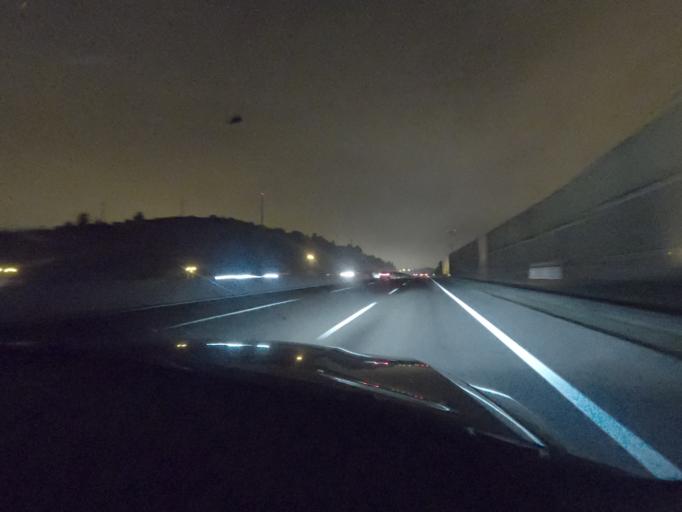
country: PT
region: Lisbon
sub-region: Vila Franca de Xira
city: Vialonga
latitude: 38.8801
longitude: -9.0629
